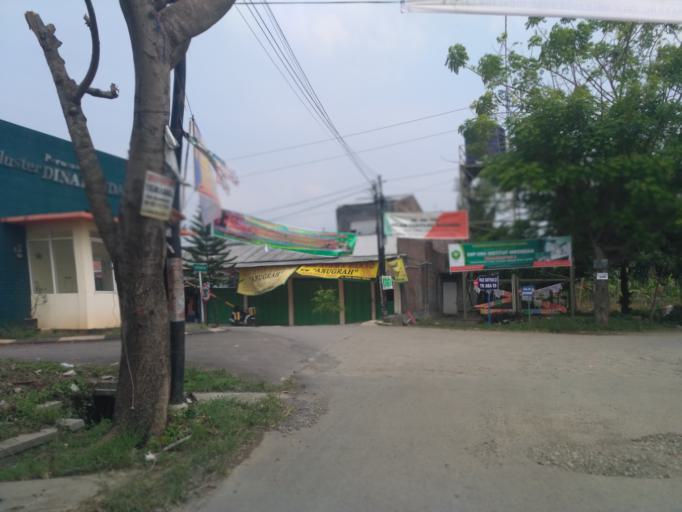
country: ID
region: Central Java
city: Mranggen
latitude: -7.0628
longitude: 110.4661
